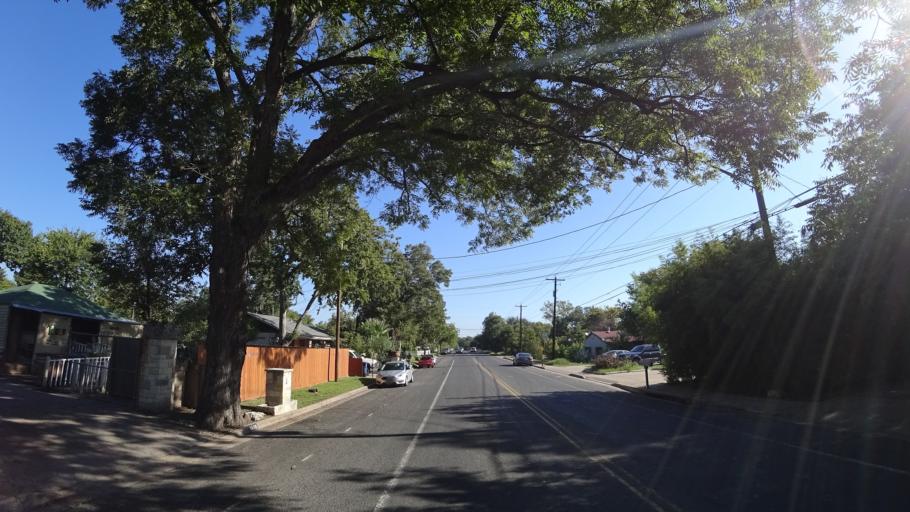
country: US
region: Texas
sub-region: Travis County
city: Austin
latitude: 30.3505
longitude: -97.7013
